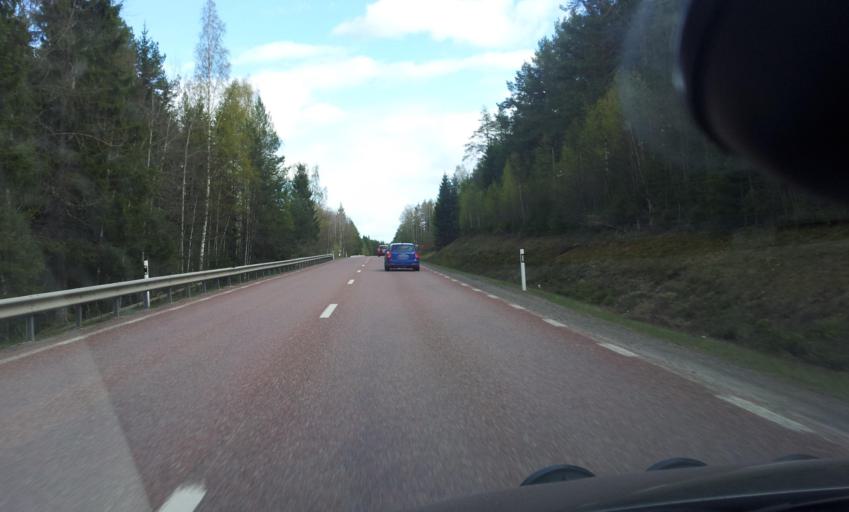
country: SE
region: Gaevleborg
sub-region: Ljusdals Kommun
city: Ljusdal
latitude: 61.8006
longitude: 16.1153
